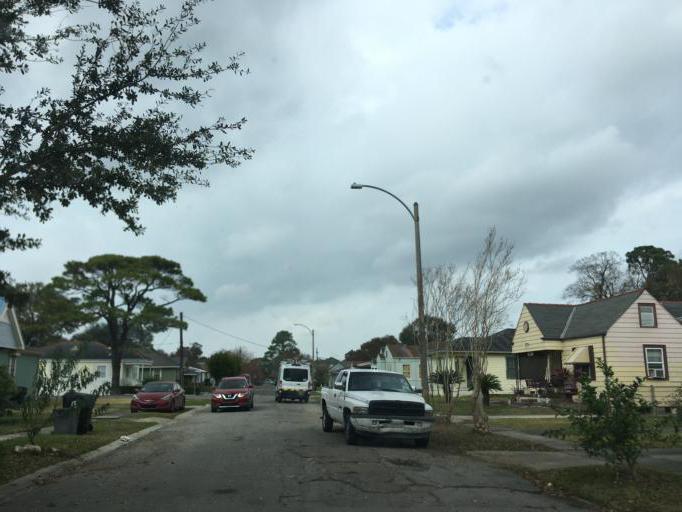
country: US
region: Louisiana
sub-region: Orleans Parish
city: New Orleans
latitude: 29.9950
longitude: -90.0552
